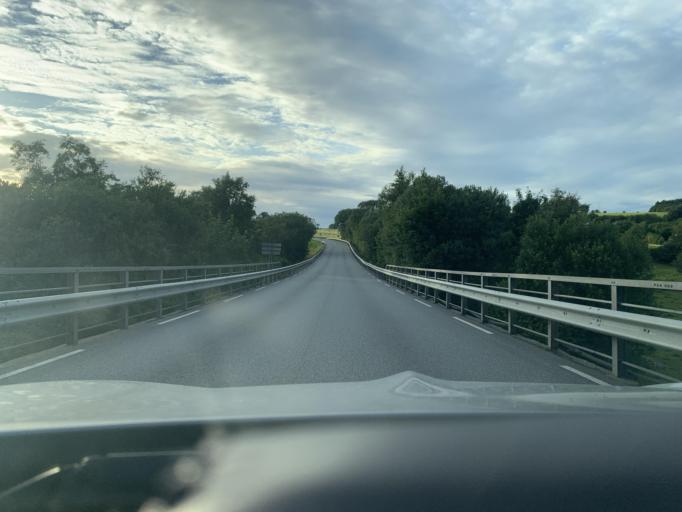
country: NO
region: Rogaland
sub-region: Time
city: Bryne
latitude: 58.7056
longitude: 5.6954
